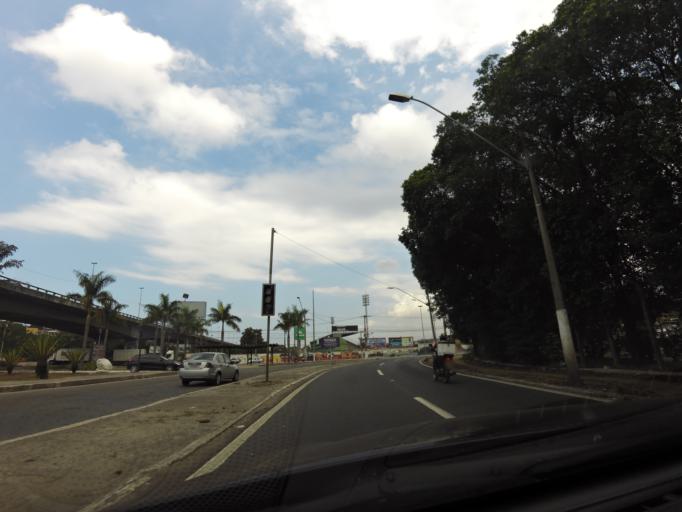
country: BR
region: Espirito Santo
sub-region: Vitoria
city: Vitoria
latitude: -20.3318
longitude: -40.3551
